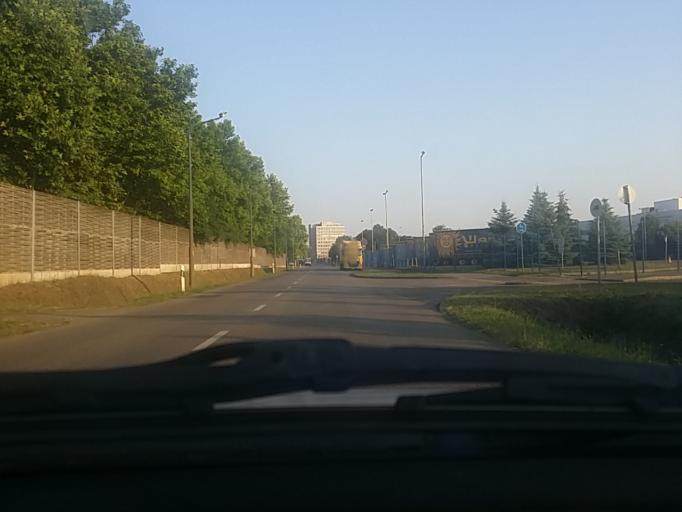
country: HU
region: Jasz-Nagykun-Szolnok
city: Jaszbereny
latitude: 47.4919
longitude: 19.8766
